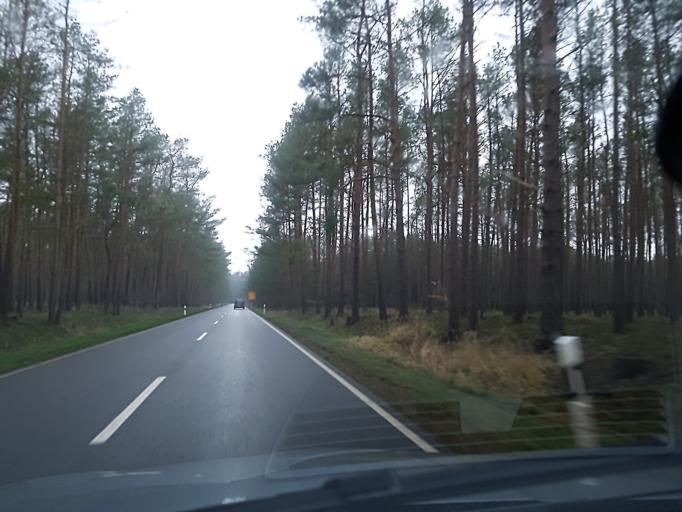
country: DE
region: Brandenburg
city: Schonborn
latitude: 51.6591
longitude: 13.5064
